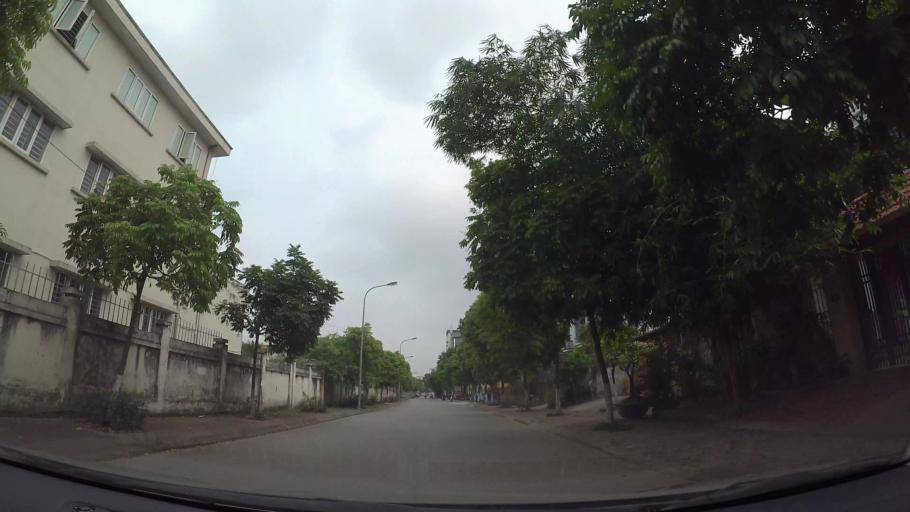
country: VN
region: Ha Noi
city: Trau Quy
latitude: 21.0441
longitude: 105.9262
